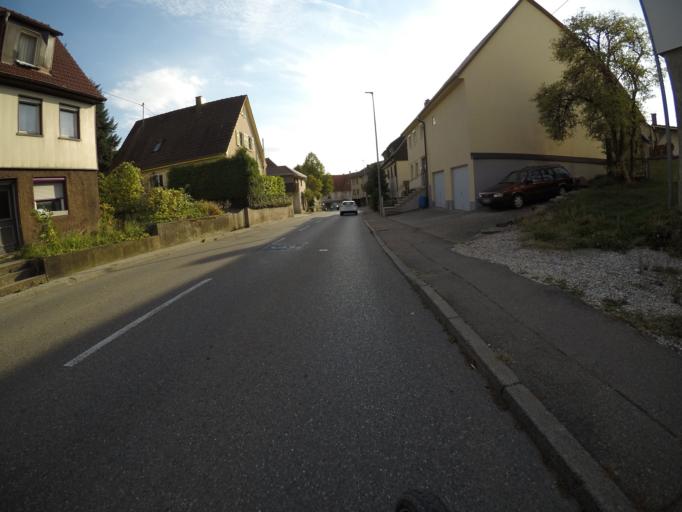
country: DE
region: Baden-Wuerttemberg
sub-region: Tuebingen Region
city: Sickenhausen
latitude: 48.5356
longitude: 9.2023
